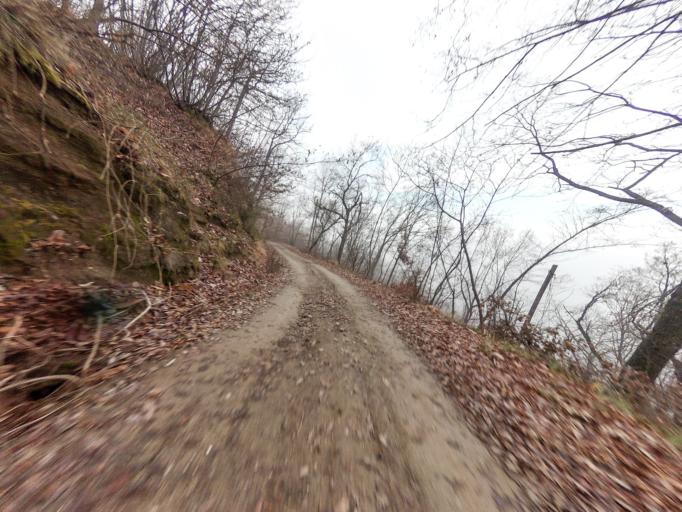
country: IT
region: Emilia-Romagna
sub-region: Provincia di Bologna
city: Monterenzio
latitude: 44.3260
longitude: 11.3498
